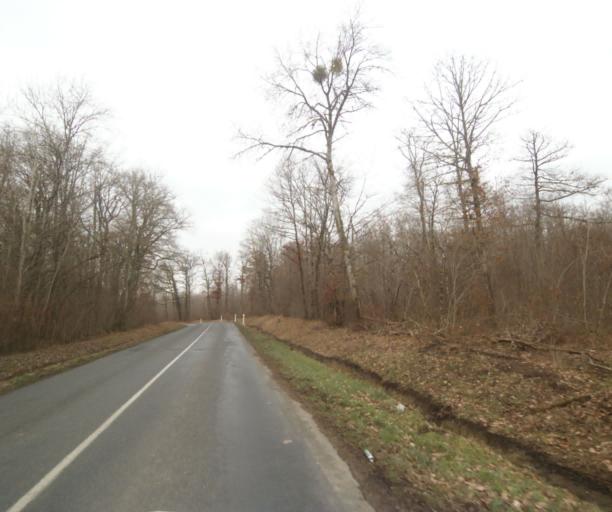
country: FR
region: Champagne-Ardenne
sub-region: Departement de la Marne
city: Pargny-sur-Saulx
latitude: 48.7314
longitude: 4.8650
